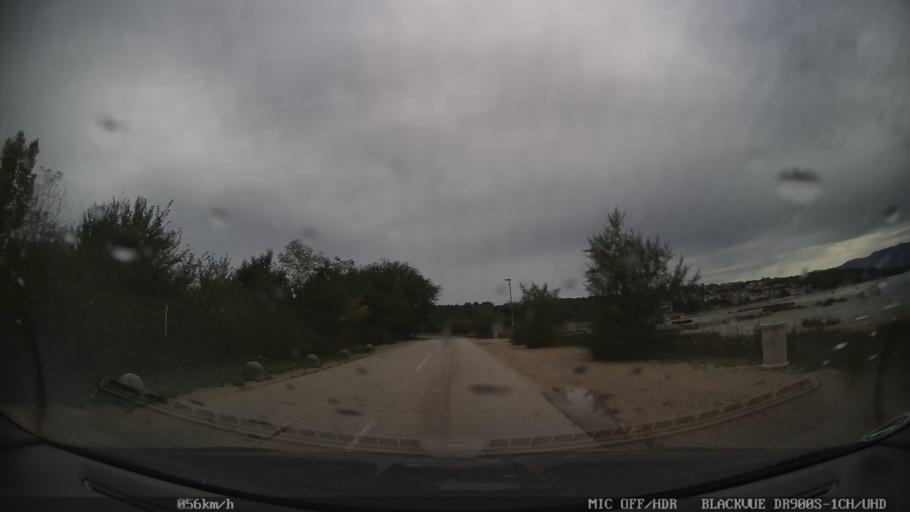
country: HR
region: Primorsko-Goranska
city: Njivice
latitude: 45.1516
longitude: 14.5995
